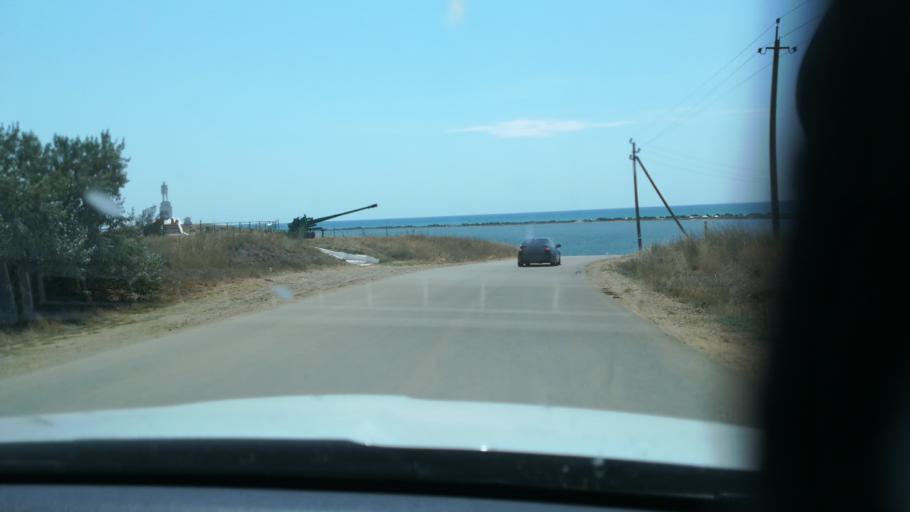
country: RU
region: Krasnodarskiy
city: Vyshestebliyevskaya
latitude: 45.1185
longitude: 36.8952
